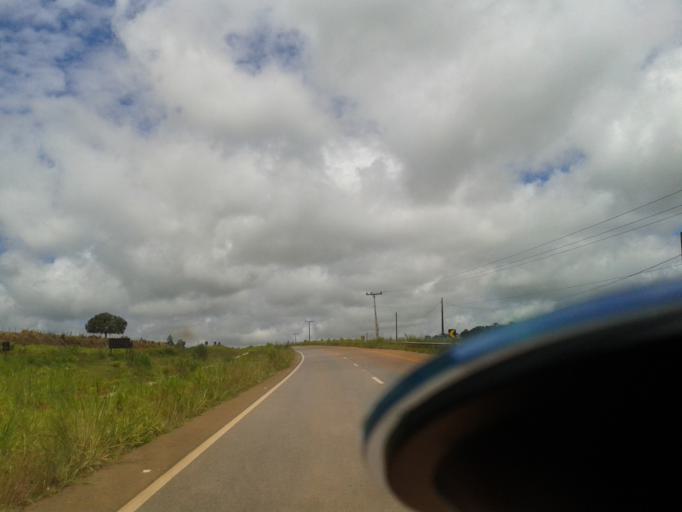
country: BR
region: Goias
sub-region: Inhumas
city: Inhumas
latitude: -16.1891
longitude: -49.6089
